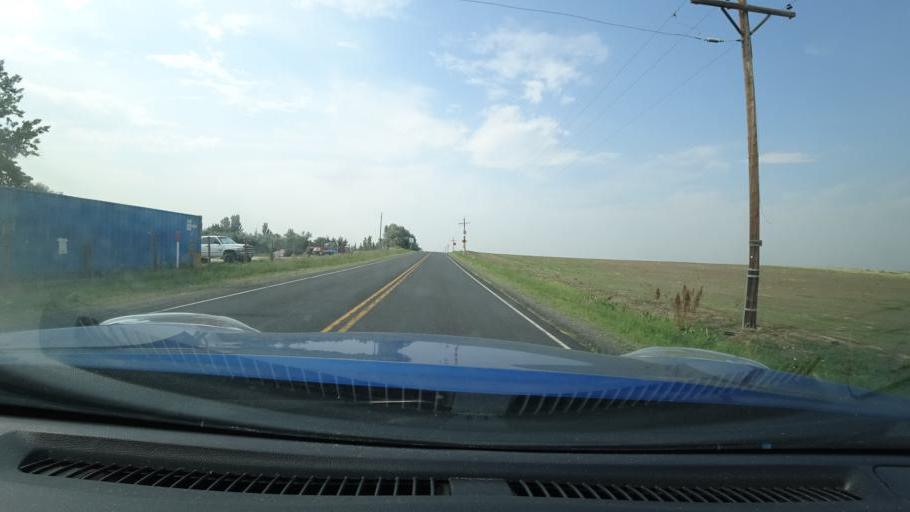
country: US
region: Colorado
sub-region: Adams County
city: Aurora
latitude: 39.7309
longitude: -104.7349
